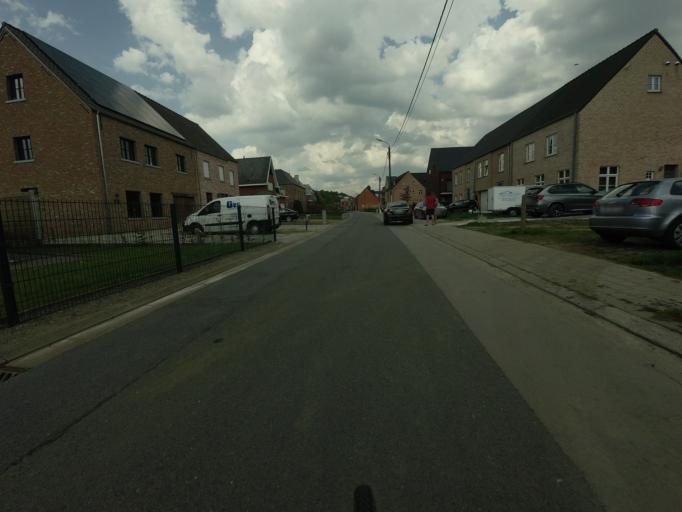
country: BE
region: Flanders
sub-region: Provincie Antwerpen
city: Putte
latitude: 51.0552
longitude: 4.6701
